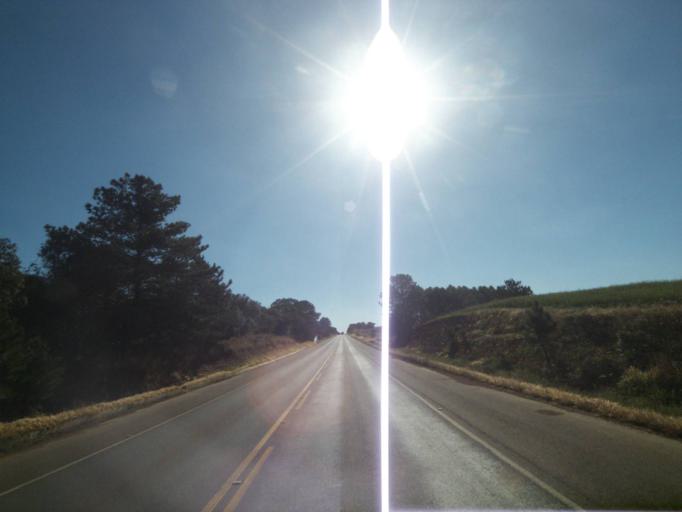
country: BR
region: Parana
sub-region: Tibagi
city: Tibagi
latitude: -24.6794
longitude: -50.4459
